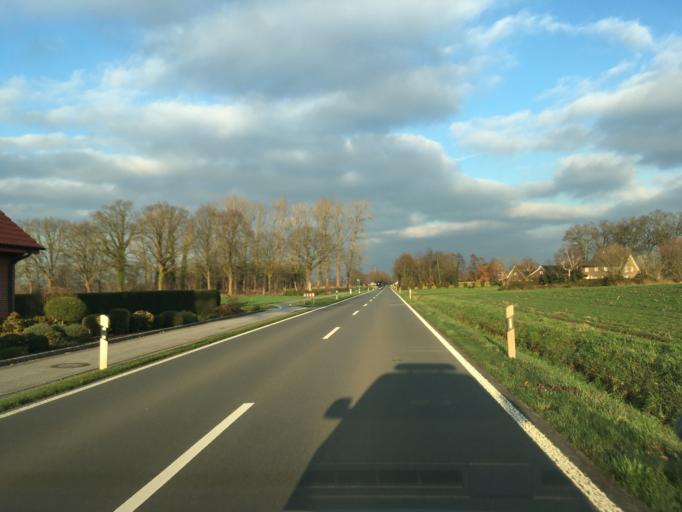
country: DE
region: North Rhine-Westphalia
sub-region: Regierungsbezirk Munster
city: Gronau
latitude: 52.1501
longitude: 7.0171
